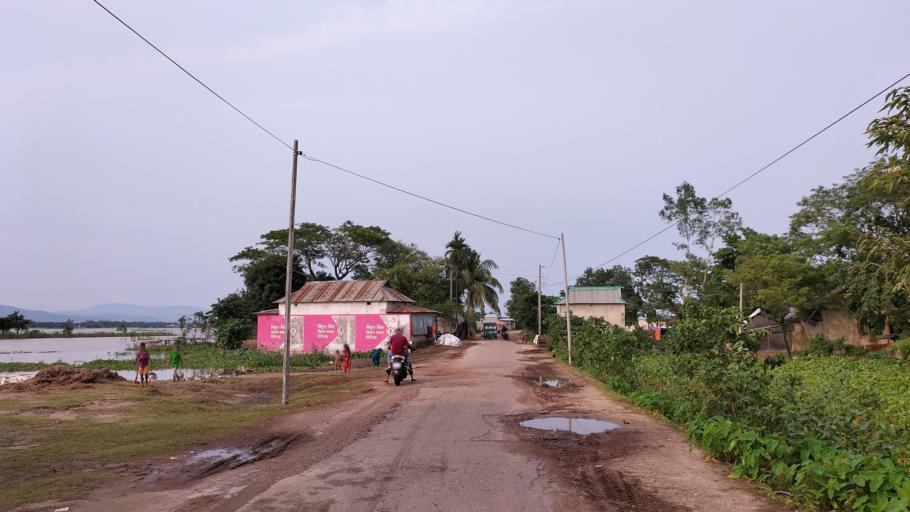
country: BD
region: Dhaka
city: Netrakona
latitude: 25.0845
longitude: 90.8974
